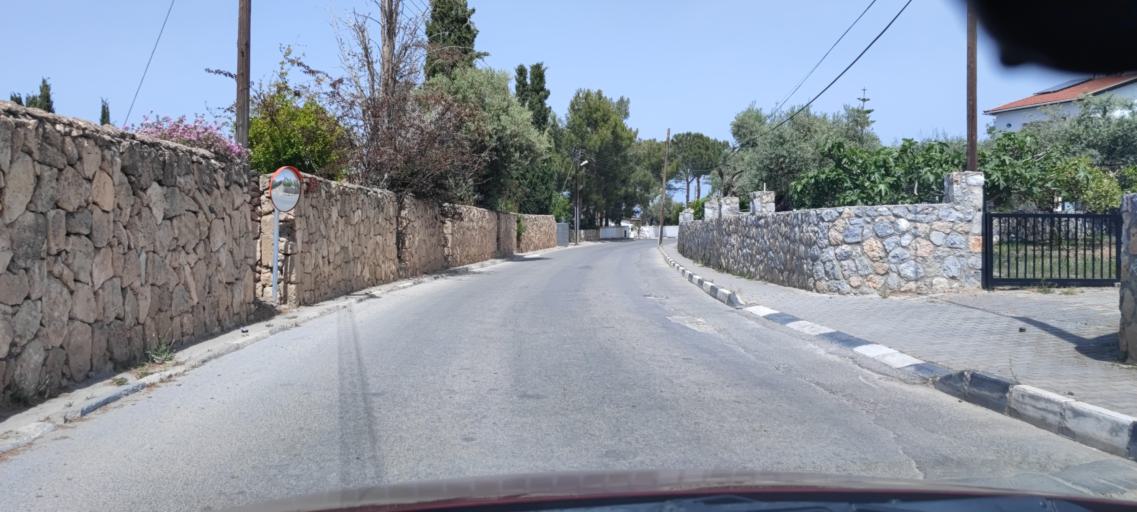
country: CY
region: Keryneia
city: Kyrenia
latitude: 35.3221
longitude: 33.3787
